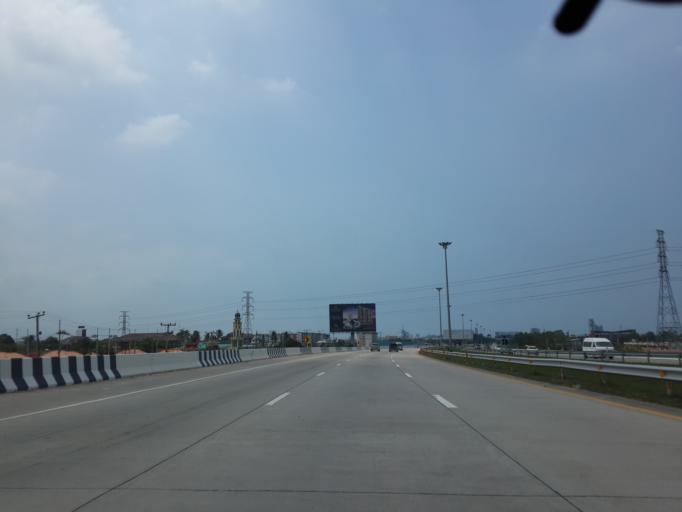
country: TH
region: Chon Buri
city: Phatthaya
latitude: 12.9461
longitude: 100.9274
